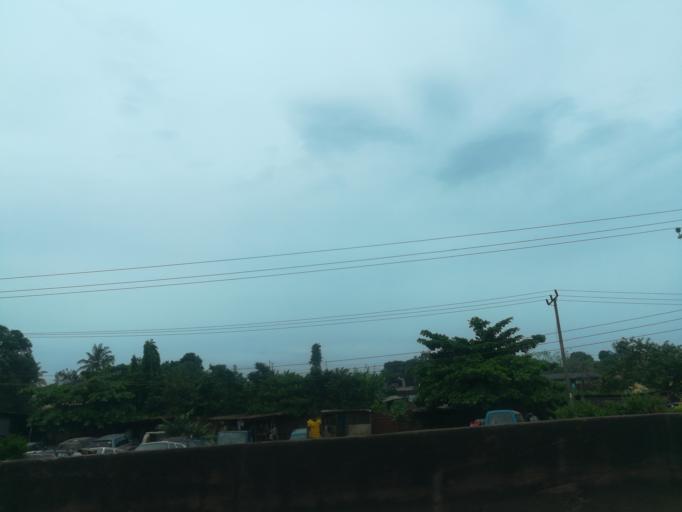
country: NG
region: Oyo
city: Ibadan
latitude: 7.3948
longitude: 3.9599
